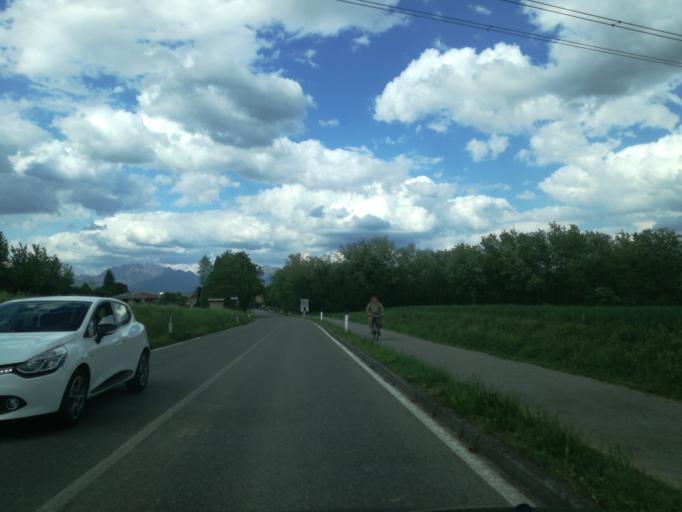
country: IT
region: Lombardy
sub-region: Provincia di Monza e Brianza
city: Ronco Briantino
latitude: 45.6628
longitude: 9.3948
